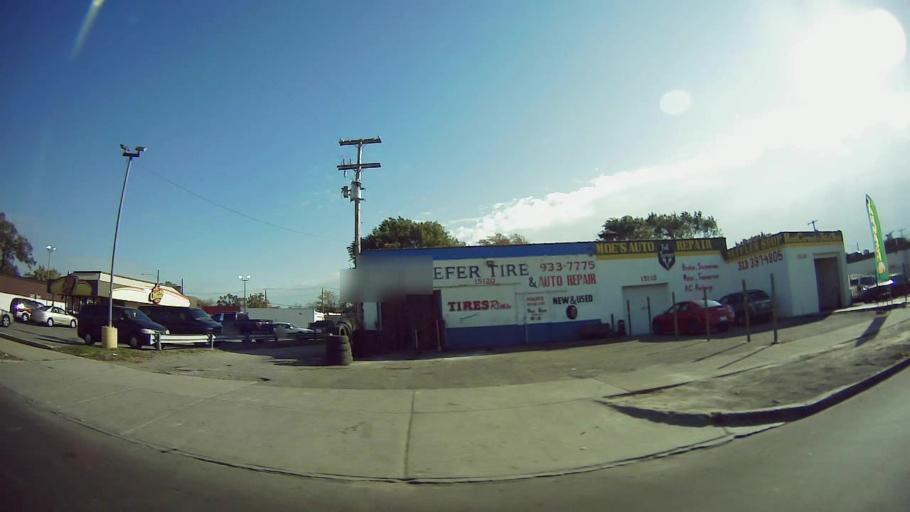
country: US
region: Michigan
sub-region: Oakland County
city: Oak Park
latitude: 42.4009
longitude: -83.1791
